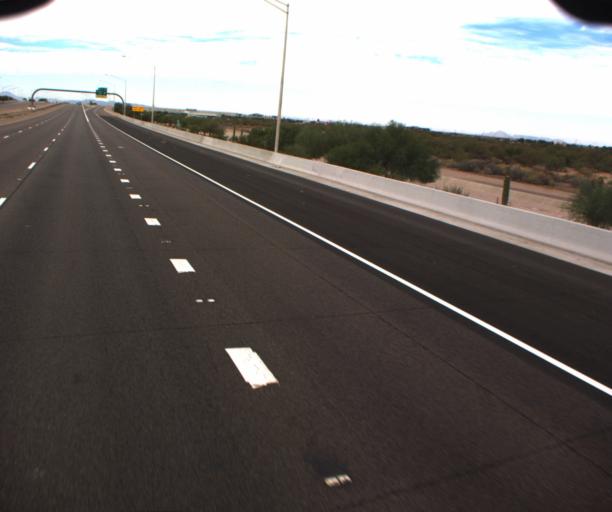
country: US
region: Arizona
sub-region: Maricopa County
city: Queen Creek
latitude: 33.3285
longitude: -111.6747
